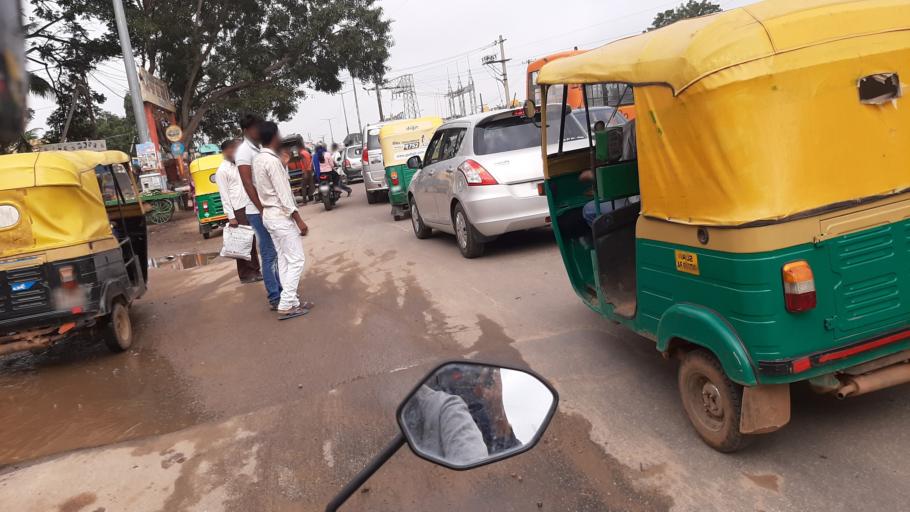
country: IN
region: Karnataka
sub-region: Bangalore Urban
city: Bangalore
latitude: 12.9850
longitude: 77.4824
